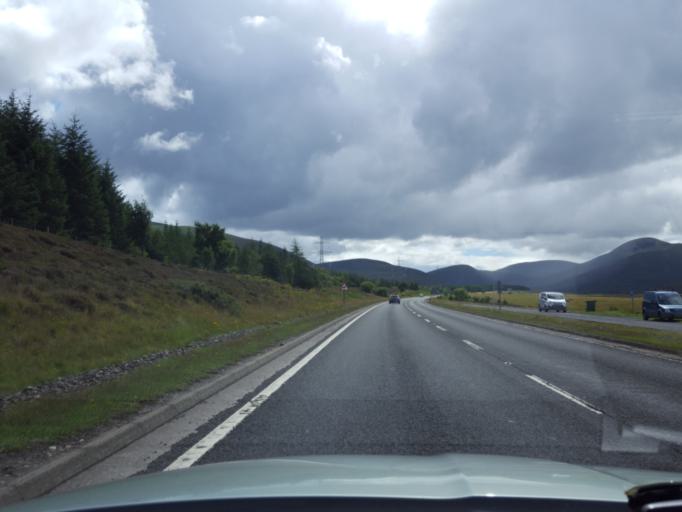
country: GB
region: Scotland
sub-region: Highland
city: Kingussie
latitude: 56.9098
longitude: -4.2360
